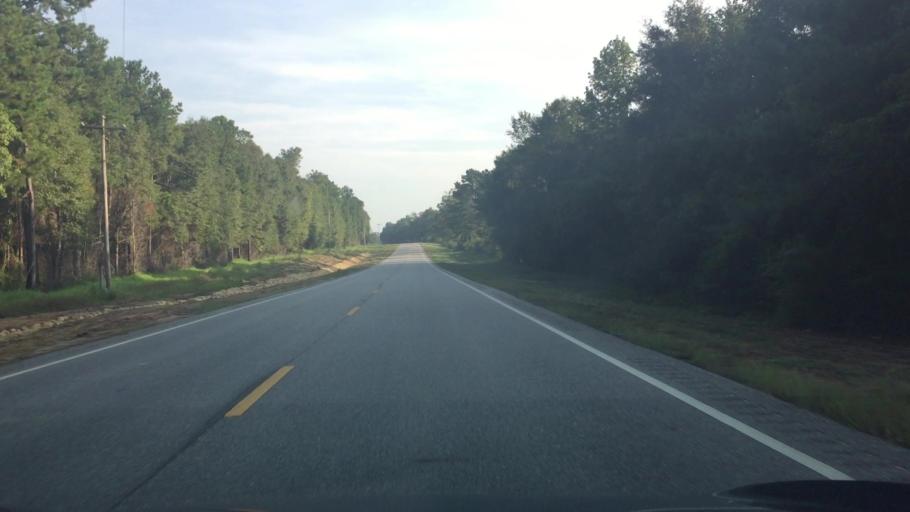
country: US
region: Alabama
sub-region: Covington County
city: Andalusia
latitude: 31.1556
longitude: -86.4585
